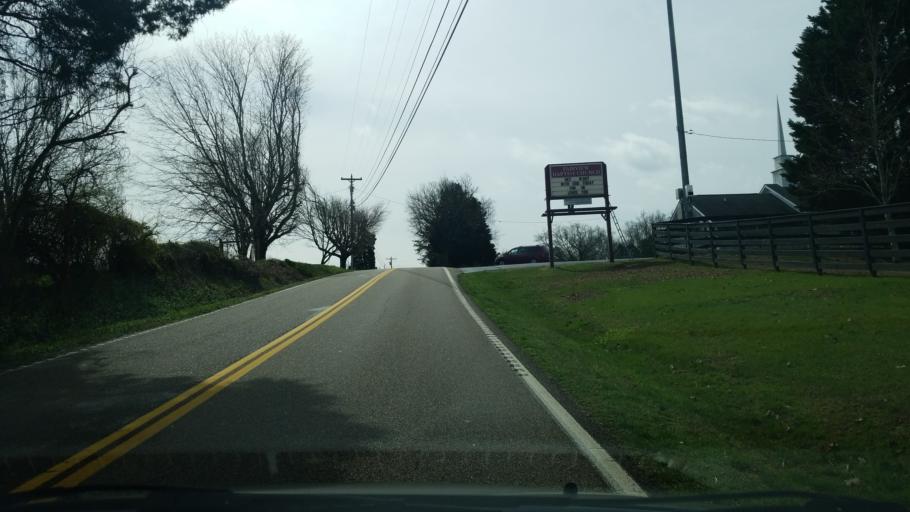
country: US
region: Tennessee
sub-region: Hamilton County
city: Collegedale
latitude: 35.1163
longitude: -85.0672
